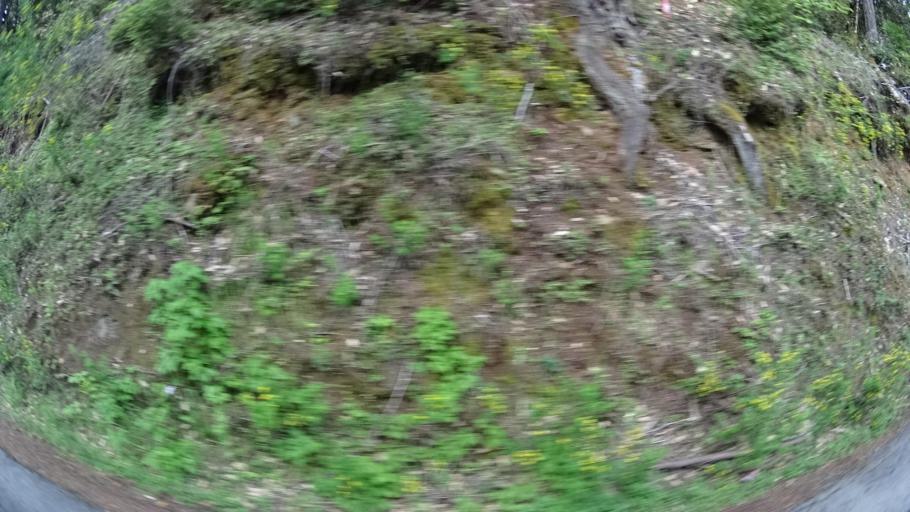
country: US
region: California
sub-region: Humboldt County
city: Redway
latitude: 40.2445
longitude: -123.8333
